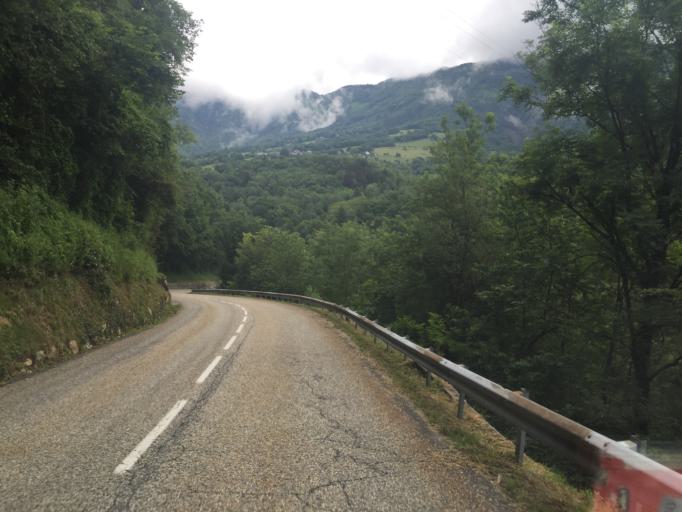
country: FR
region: Rhone-Alpes
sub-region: Departement de la Savoie
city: Barby
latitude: 45.5892
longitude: 6.0192
